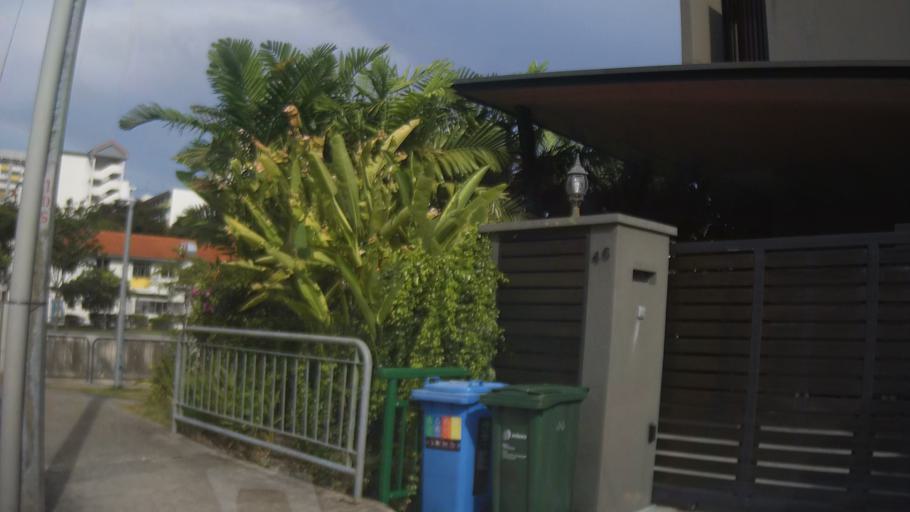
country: SG
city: Singapore
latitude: 1.3284
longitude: 103.8846
